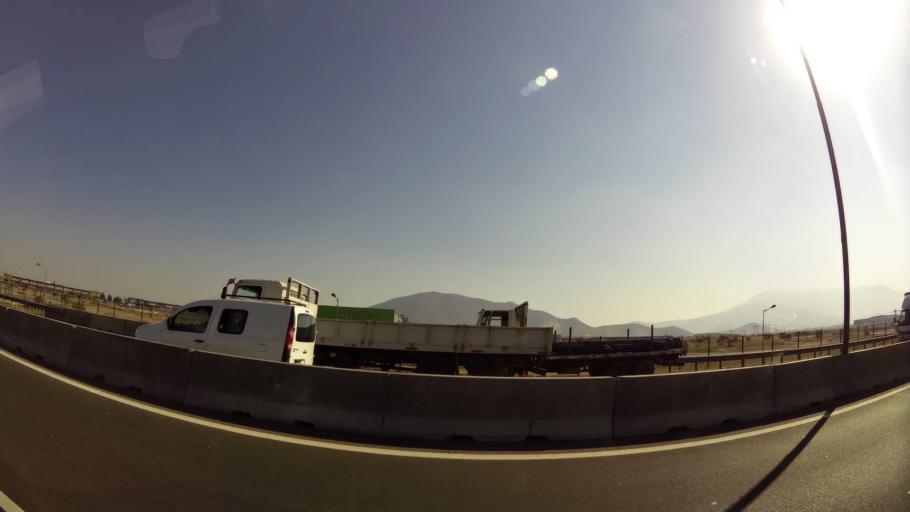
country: CL
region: Santiago Metropolitan
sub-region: Provincia de Santiago
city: Lo Prado
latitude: -33.4385
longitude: -70.7832
